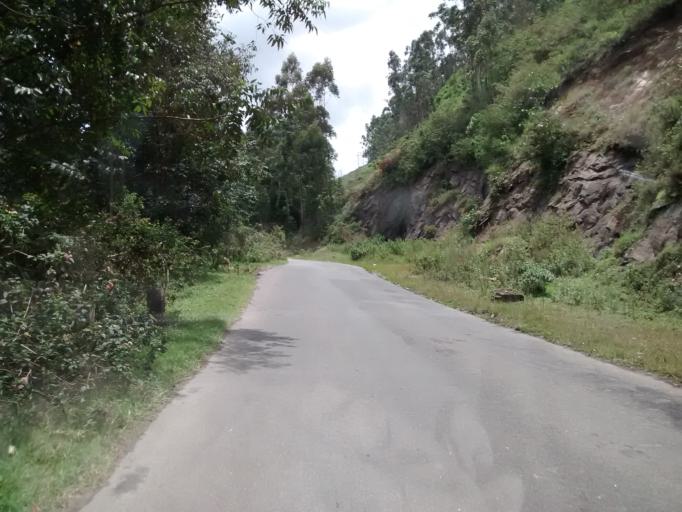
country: IN
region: Kerala
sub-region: Idukki
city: Munnar
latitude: 10.1252
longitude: 77.1621
